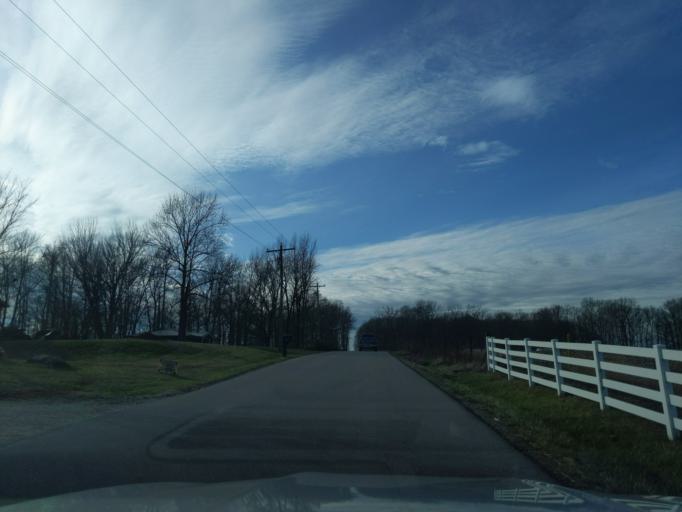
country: US
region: Indiana
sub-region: Decatur County
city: Westport
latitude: 39.1909
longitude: -85.5412
